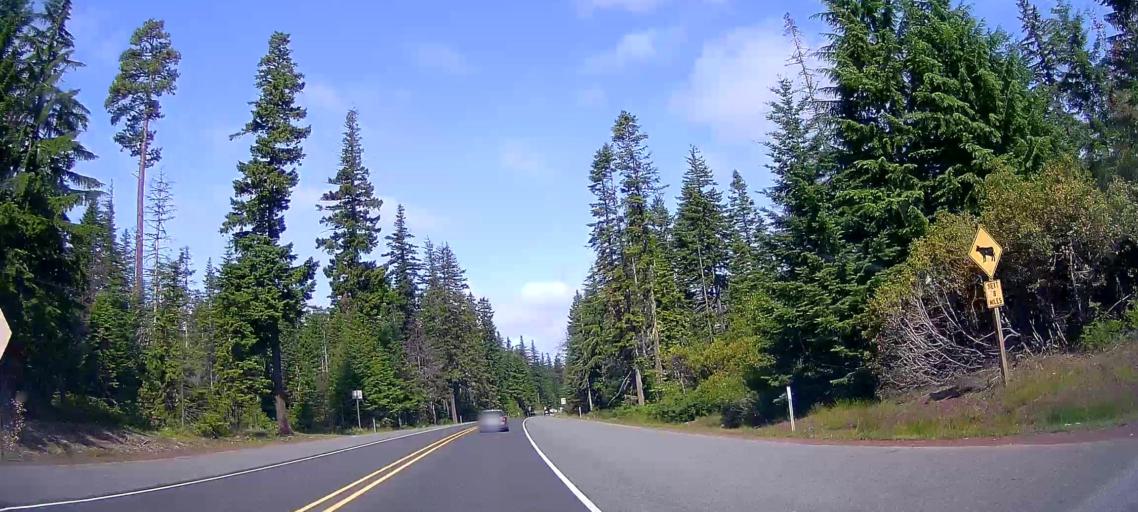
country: US
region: Oregon
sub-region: Clackamas County
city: Mount Hood Village
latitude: 45.1324
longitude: -121.6075
